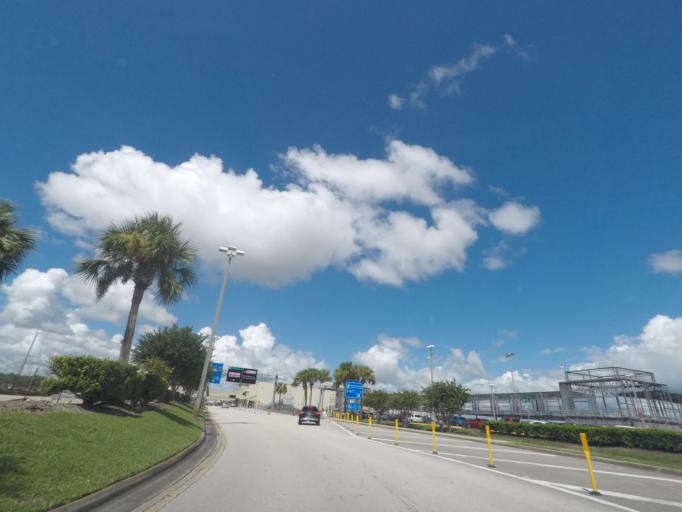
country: US
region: Florida
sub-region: Seminole County
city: Midway
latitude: 28.7751
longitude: -81.2403
